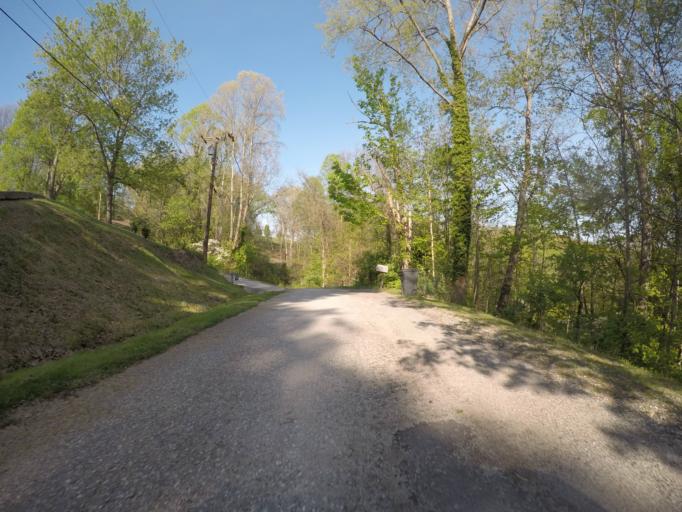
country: US
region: West Virginia
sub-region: Kanawha County
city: Charleston
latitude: 38.3905
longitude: -81.6083
